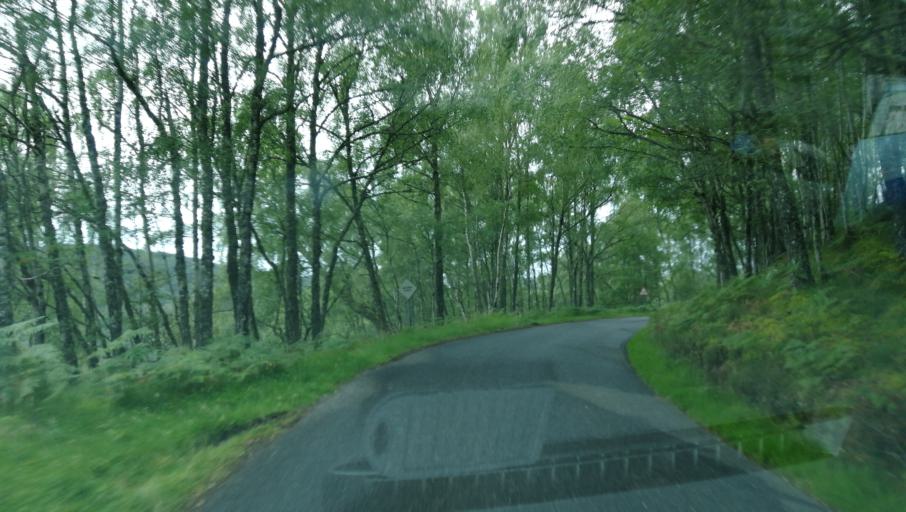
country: GB
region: Scotland
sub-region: Highland
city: Beauly
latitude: 57.3174
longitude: -4.8161
